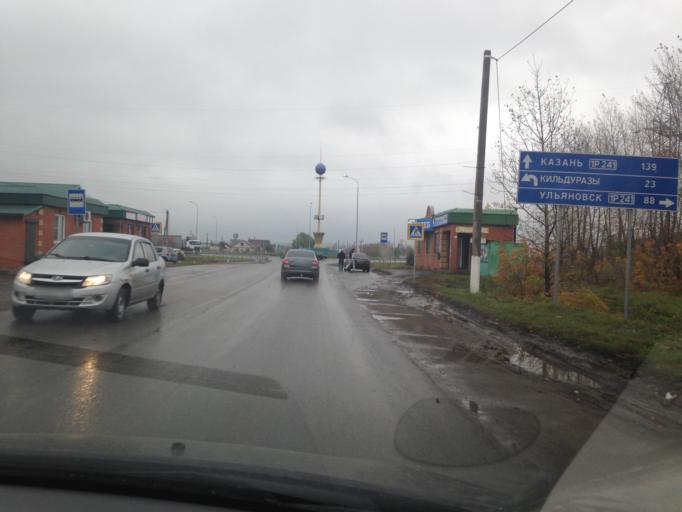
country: RU
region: Tatarstan
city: Buinsk
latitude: 54.9901
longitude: 48.3170
